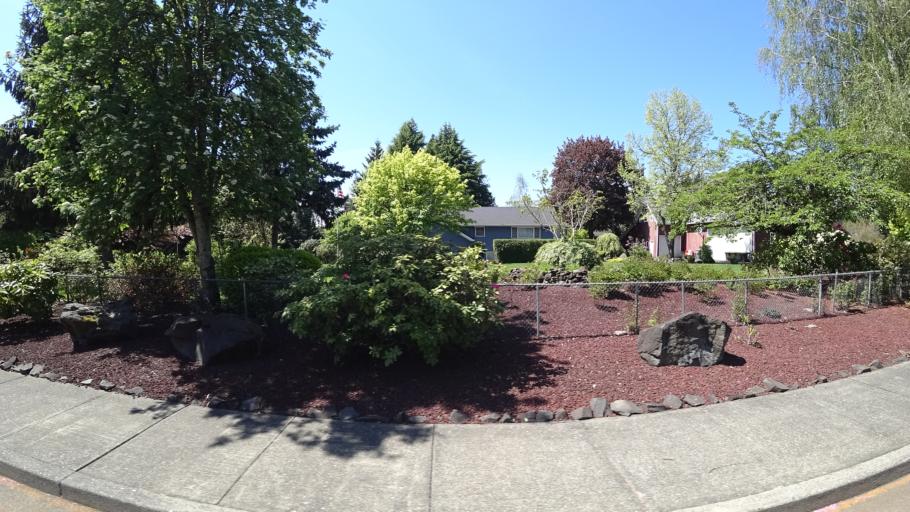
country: US
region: Oregon
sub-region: Washington County
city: Hillsboro
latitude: 45.5190
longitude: -122.9612
